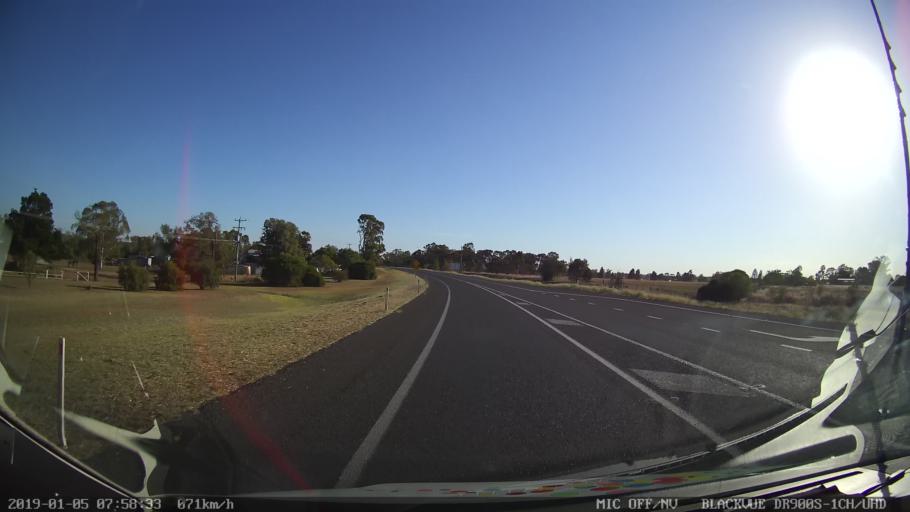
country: AU
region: New South Wales
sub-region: Gilgandra
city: Gilgandra
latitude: -31.7112
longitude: 148.6760
